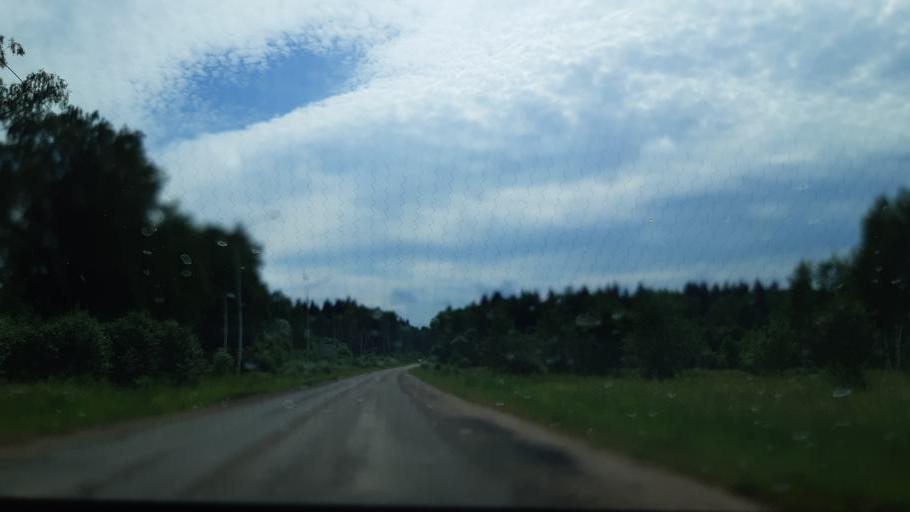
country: RU
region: Moskovskaya
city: Vereya
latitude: 55.2401
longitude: 36.0409
